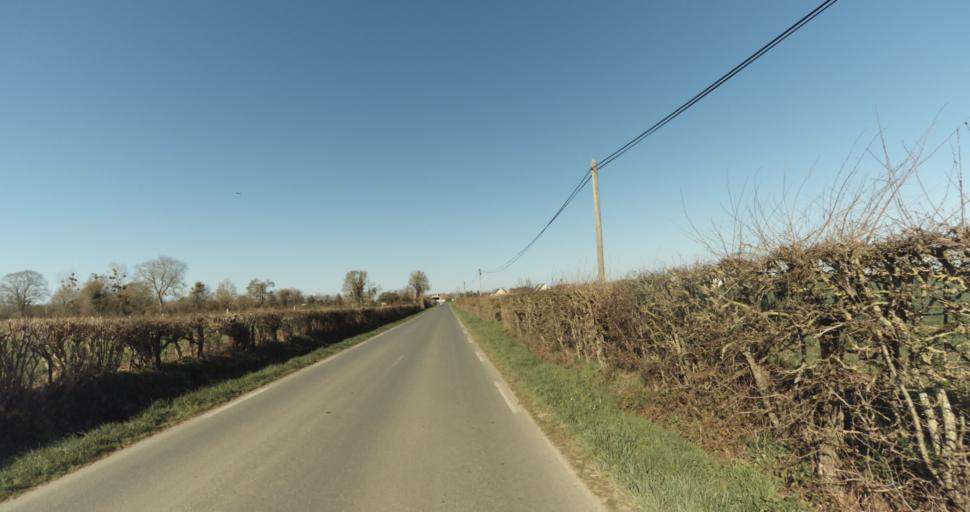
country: FR
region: Lower Normandy
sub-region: Departement du Calvados
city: Saint-Pierre-sur-Dives
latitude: 48.9897
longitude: -0.0111
